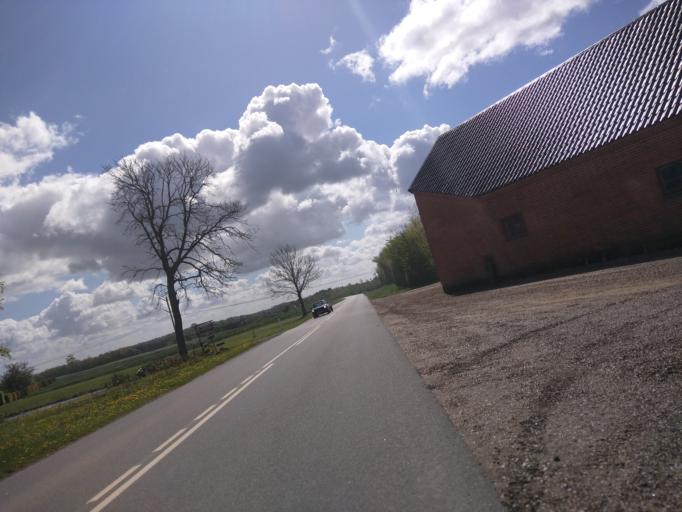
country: DK
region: Central Jutland
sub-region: Silkeborg Kommune
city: Kjellerup
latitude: 56.2813
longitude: 9.4815
